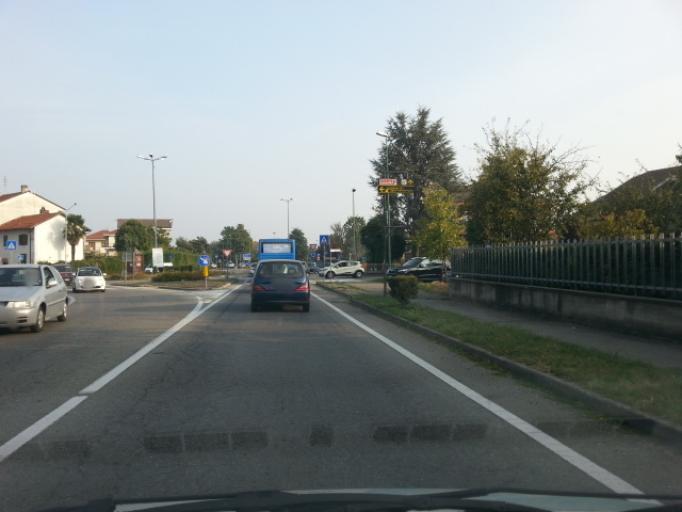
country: IT
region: Piedmont
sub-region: Provincia di Torino
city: Bruino
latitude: 45.0206
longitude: 7.4640
